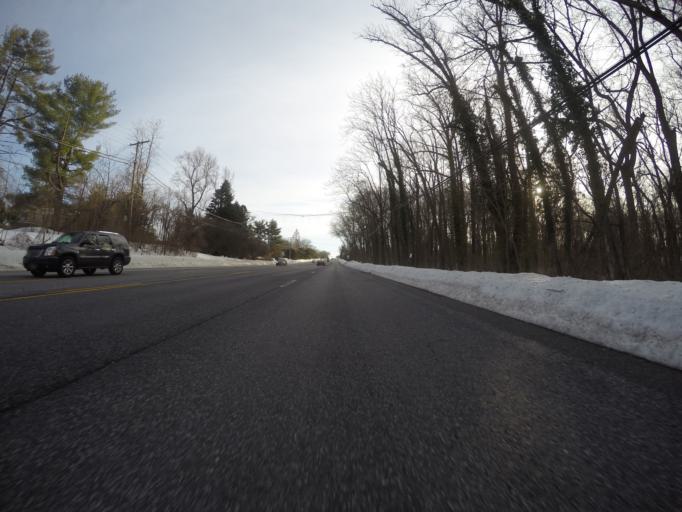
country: US
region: Maryland
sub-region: Baltimore County
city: Hampton
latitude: 39.4202
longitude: -76.5984
